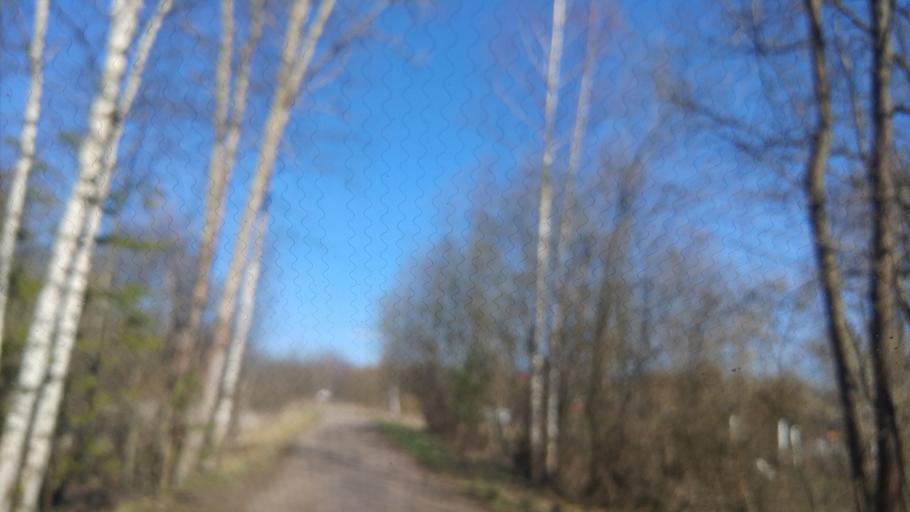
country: RU
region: Moskovskaya
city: Khot'kovo
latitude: 56.1907
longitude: 38.0292
